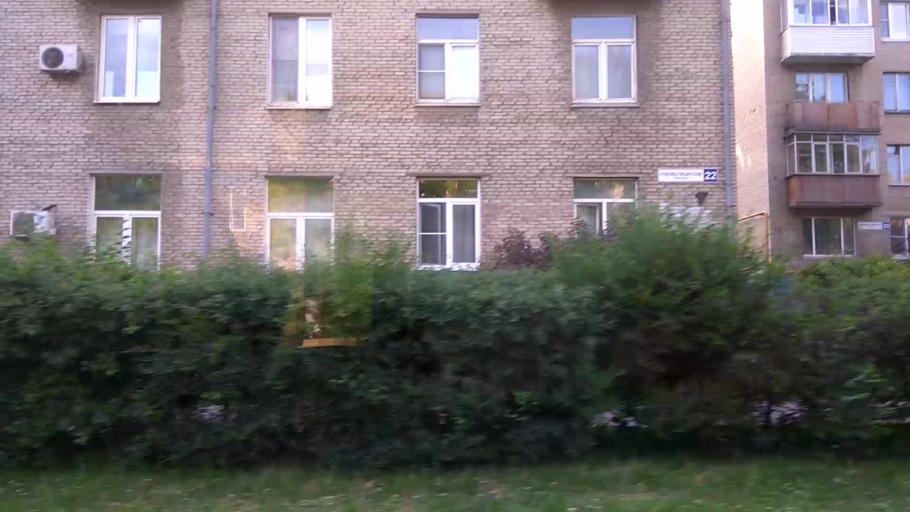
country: RU
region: Moskovskaya
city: Mytishchi
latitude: 55.9139
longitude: 37.7425
